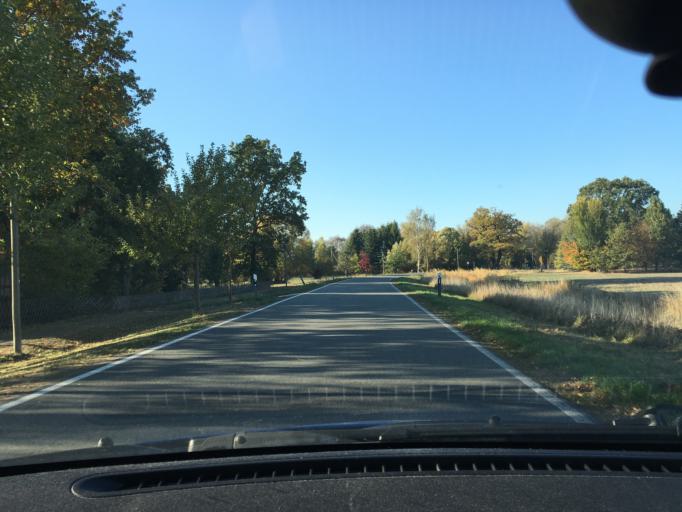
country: DE
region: Lower Saxony
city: Hitzacker
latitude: 53.1678
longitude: 11.0374
